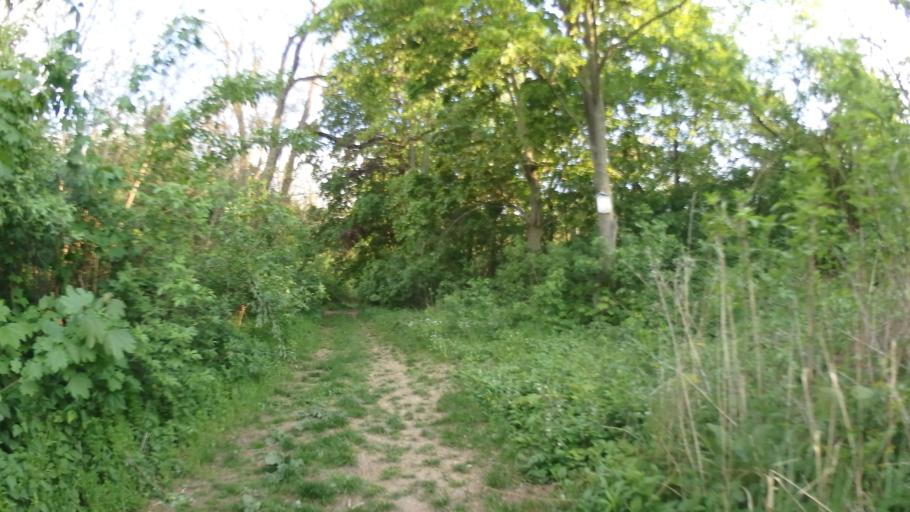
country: CZ
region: South Moravian
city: Moravany
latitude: 49.1331
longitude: 16.5807
